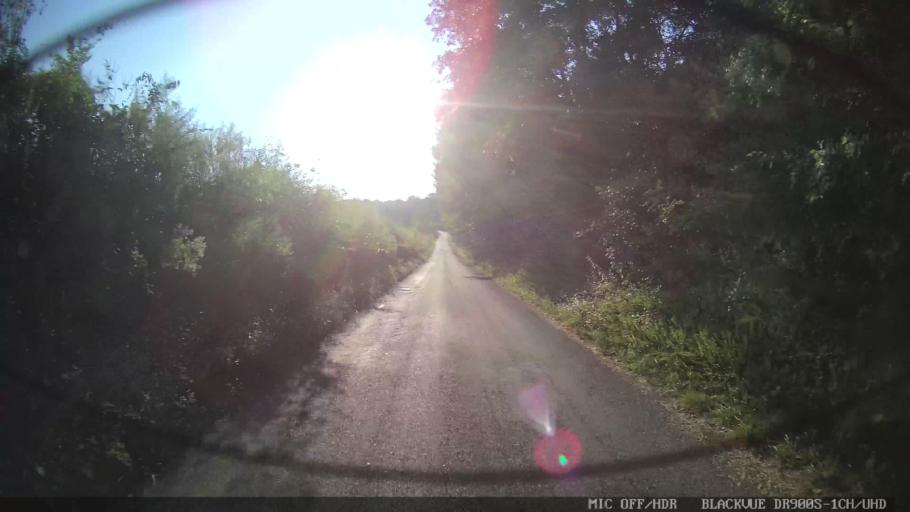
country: US
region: Tennessee
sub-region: Bradley County
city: Wildwood Lake
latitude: 35.0145
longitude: -84.7396
